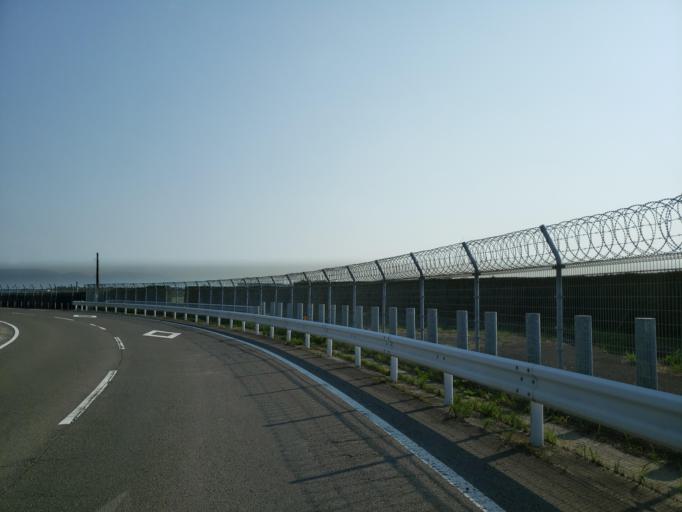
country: JP
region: Ehime
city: Masaki-cho
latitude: 33.8268
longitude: 132.7053
